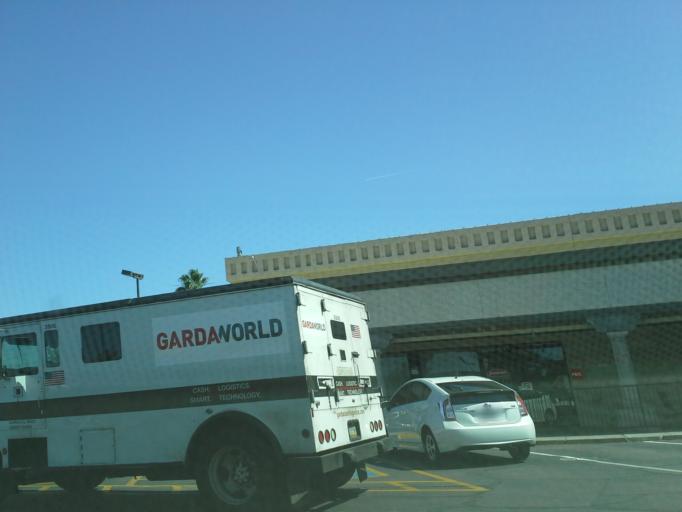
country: US
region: Arizona
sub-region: Maricopa County
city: Paradise Valley
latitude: 33.5831
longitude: -111.9255
